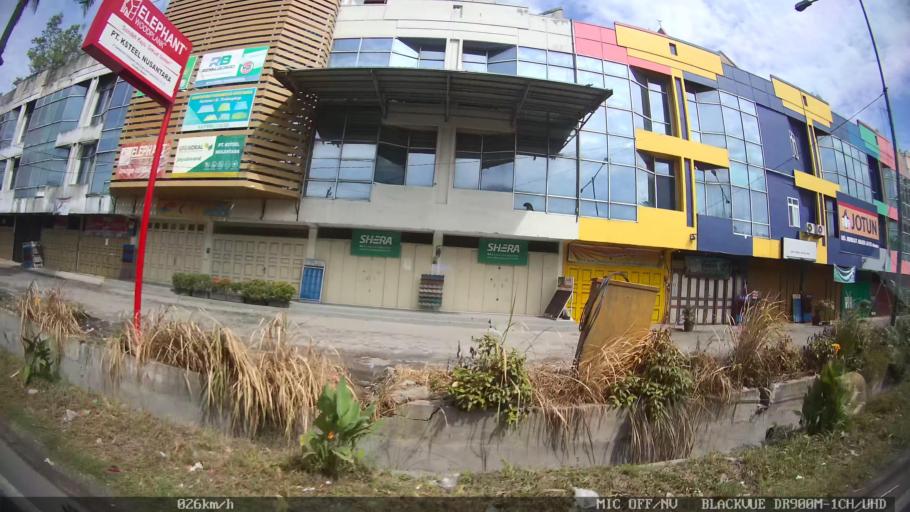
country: ID
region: North Sumatra
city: Medan
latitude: 3.6215
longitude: 98.6586
